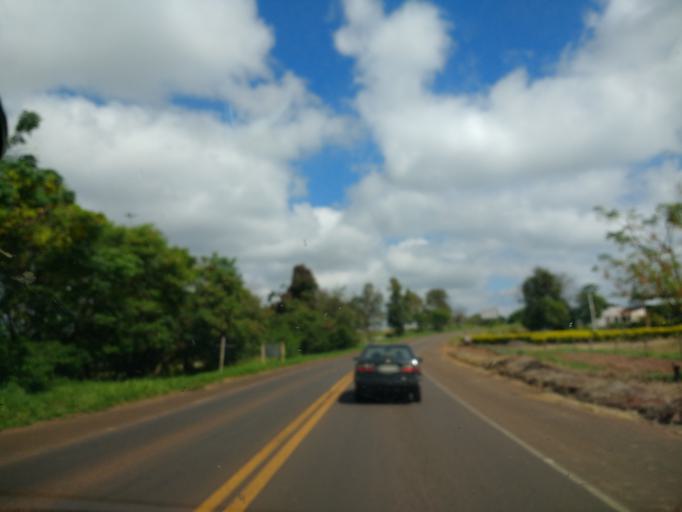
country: BR
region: Parana
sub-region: Cruzeiro Do Oeste
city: Cruzeiro do Oeste
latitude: -23.7969
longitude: -53.0497
